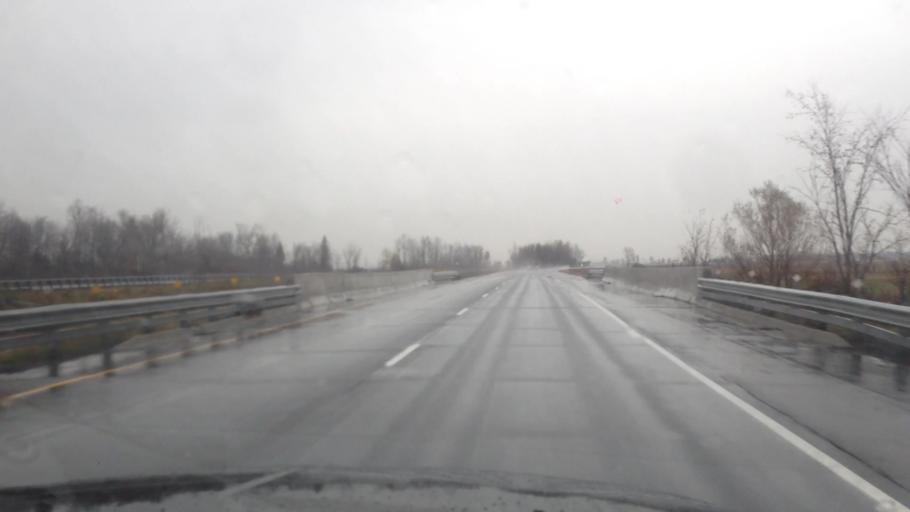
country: CA
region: Ontario
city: Casselman
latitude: 45.3535
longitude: -74.8877
